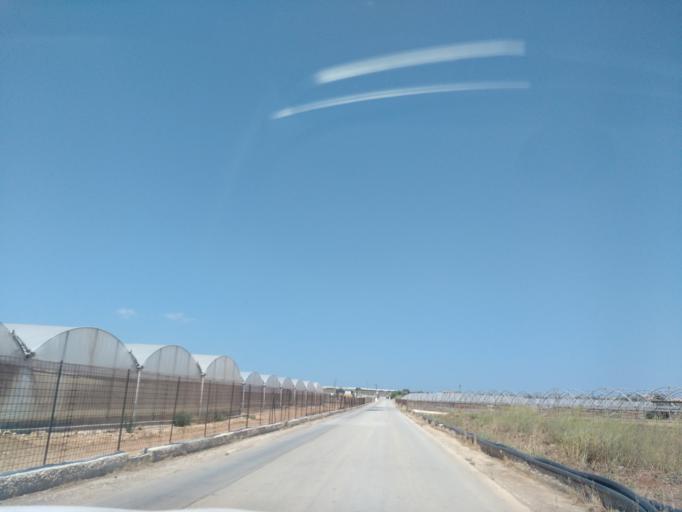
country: IT
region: Sicily
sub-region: Provincia di Siracusa
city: Pachino
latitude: 36.6712
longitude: 15.0839
